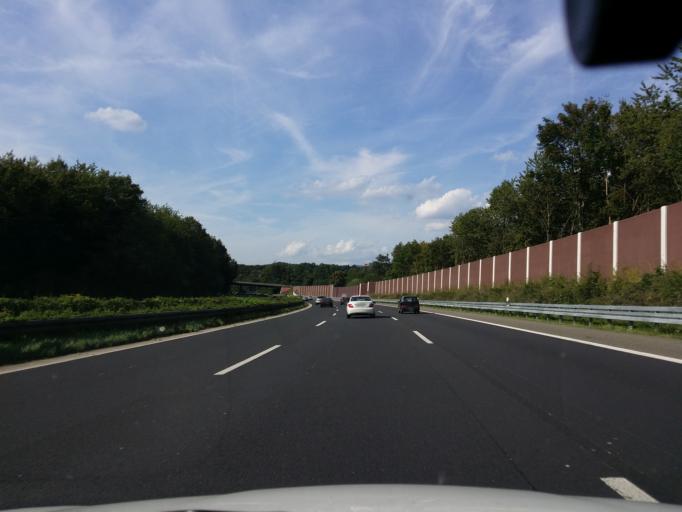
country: DE
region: North Rhine-Westphalia
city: Lohmar
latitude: 50.8554
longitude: 7.2150
